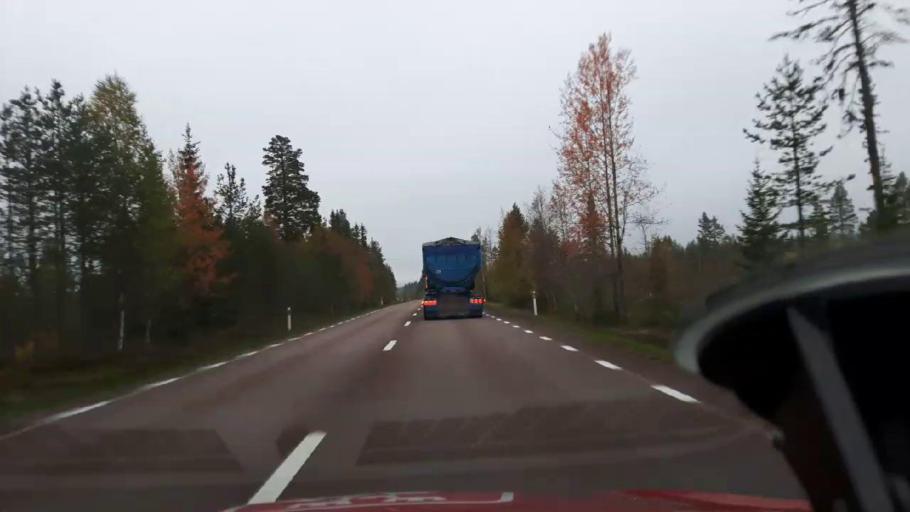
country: SE
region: Jaemtland
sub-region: Bergs Kommun
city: Hoverberg
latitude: 62.5957
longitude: 14.4233
